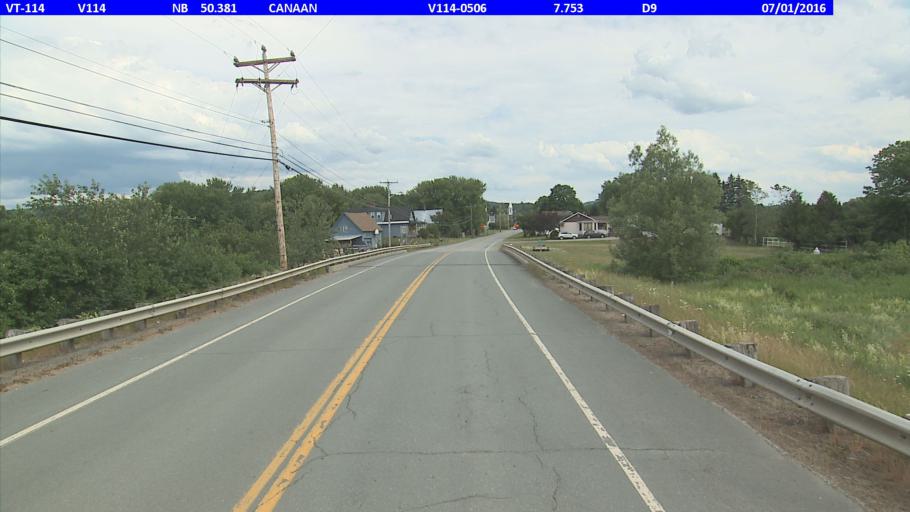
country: US
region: New Hampshire
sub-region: Coos County
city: Colebrook
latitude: 45.0002
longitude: -71.5450
